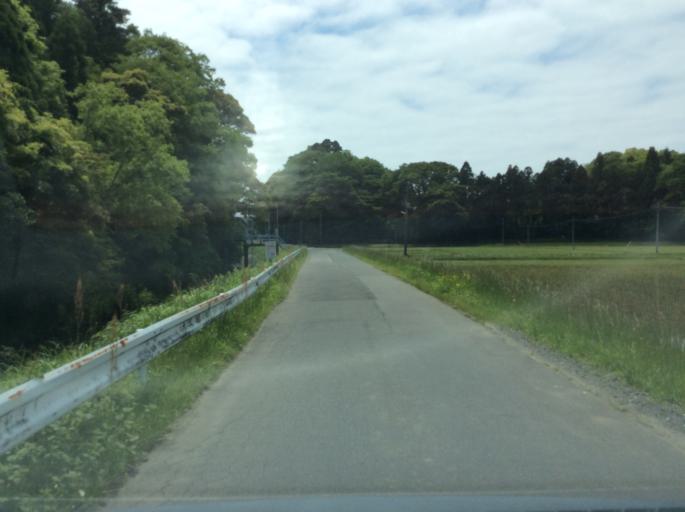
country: JP
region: Fukushima
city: Iwaki
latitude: 37.0240
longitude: 140.9380
